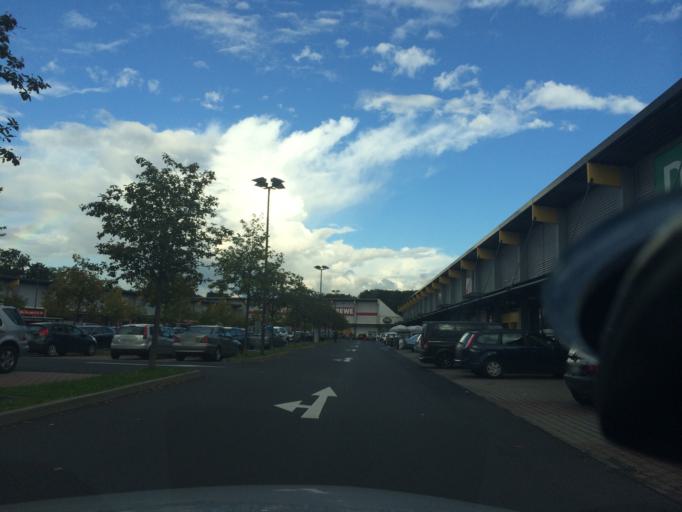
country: DE
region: Hesse
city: Morfelden-Walldorf
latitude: 50.0116
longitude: 8.5857
